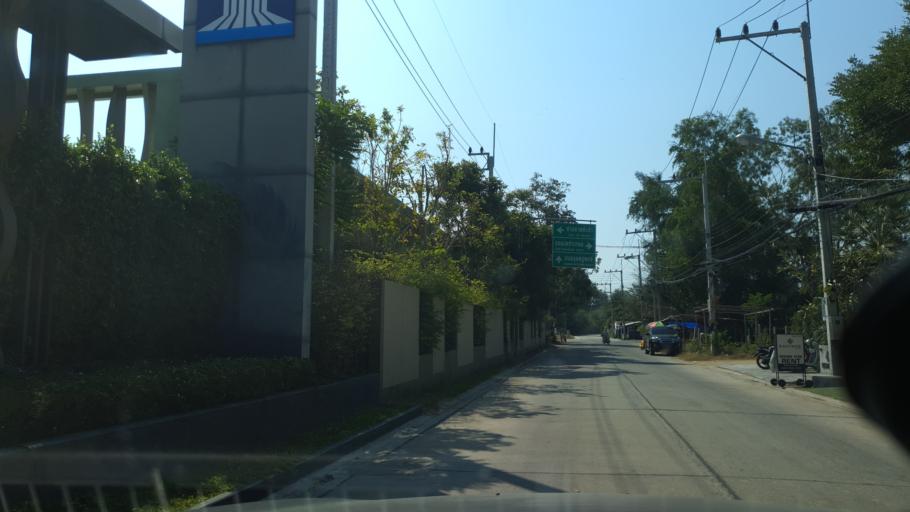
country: TH
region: Phetchaburi
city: Cha-am
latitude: 12.7793
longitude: 99.9763
